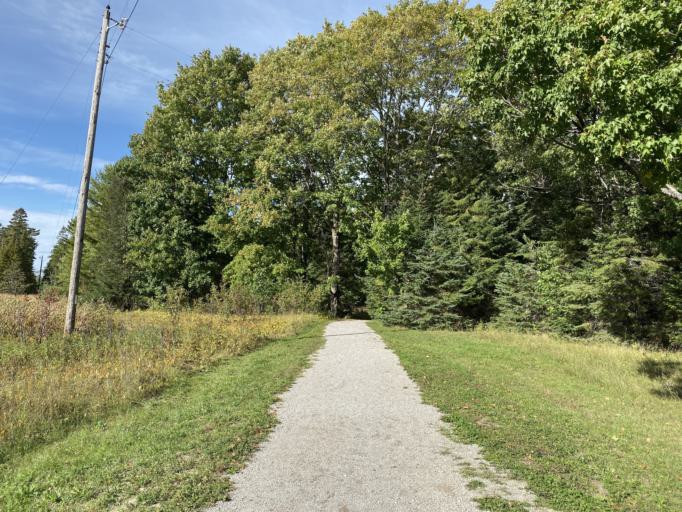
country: US
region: Michigan
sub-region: Mackinac County
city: Saint Ignace
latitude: 45.7435
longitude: -84.8975
